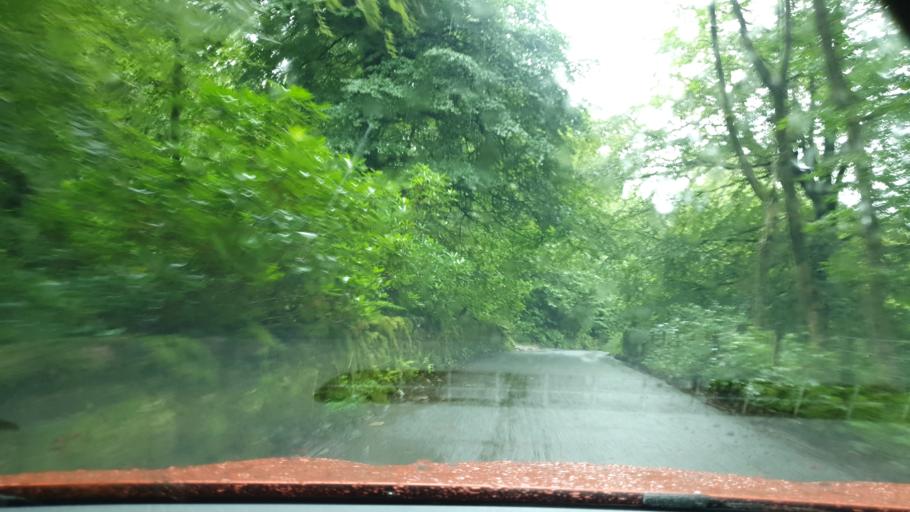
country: GB
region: England
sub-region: Cumbria
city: Seascale
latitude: 54.4297
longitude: -3.3193
